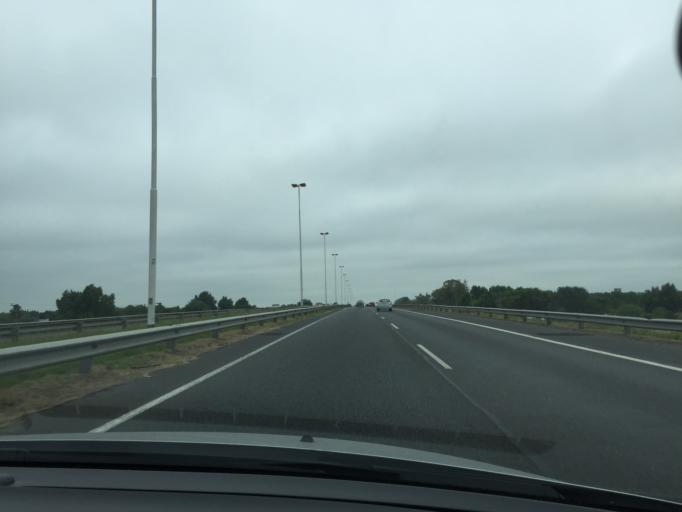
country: AR
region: Buenos Aires
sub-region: Partido de Ezeiza
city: Ezeiza
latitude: -34.8487
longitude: -58.5419
